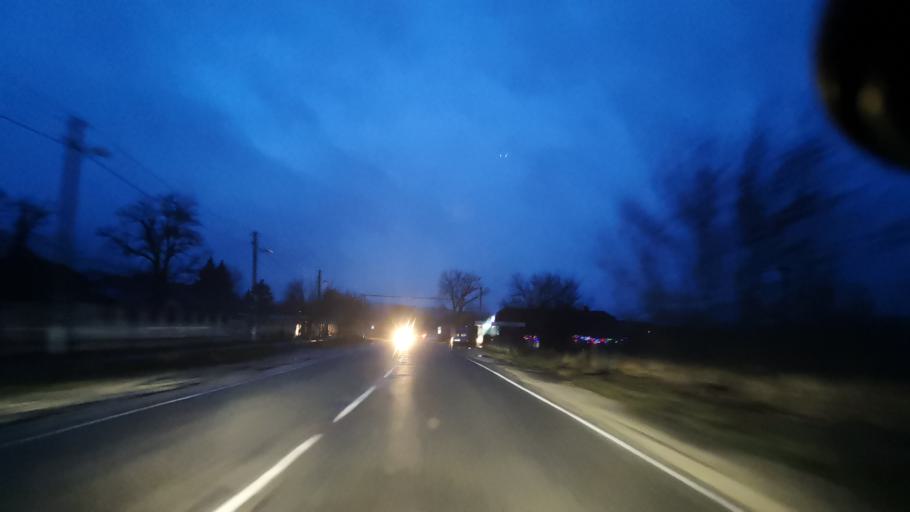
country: MD
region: Orhei
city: Orhei
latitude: 47.4550
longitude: 28.7917
